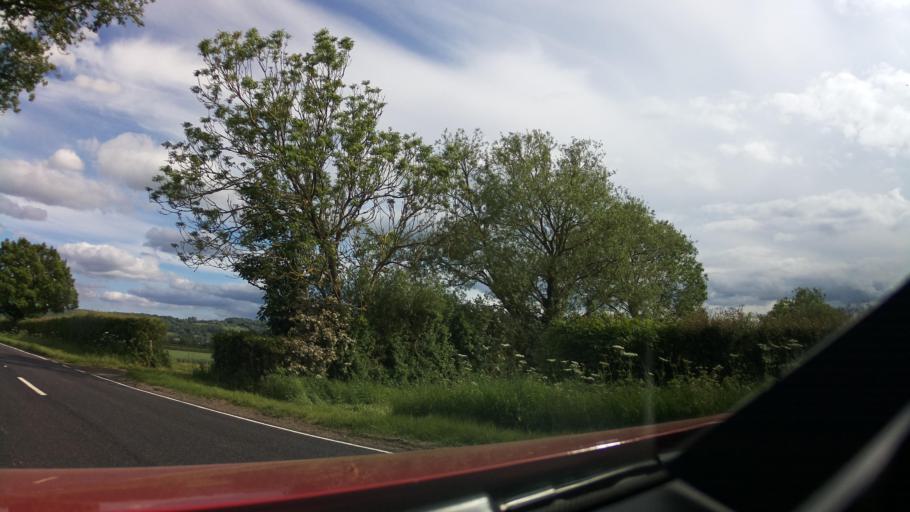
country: GB
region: England
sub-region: Worcestershire
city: Broadway
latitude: 52.0797
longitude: -1.8470
